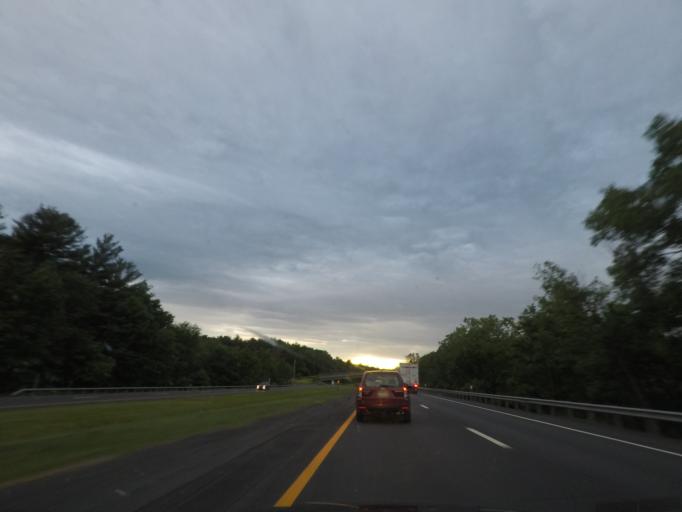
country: US
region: New York
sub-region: Rensselaer County
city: Nassau
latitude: 42.4458
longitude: -73.5636
